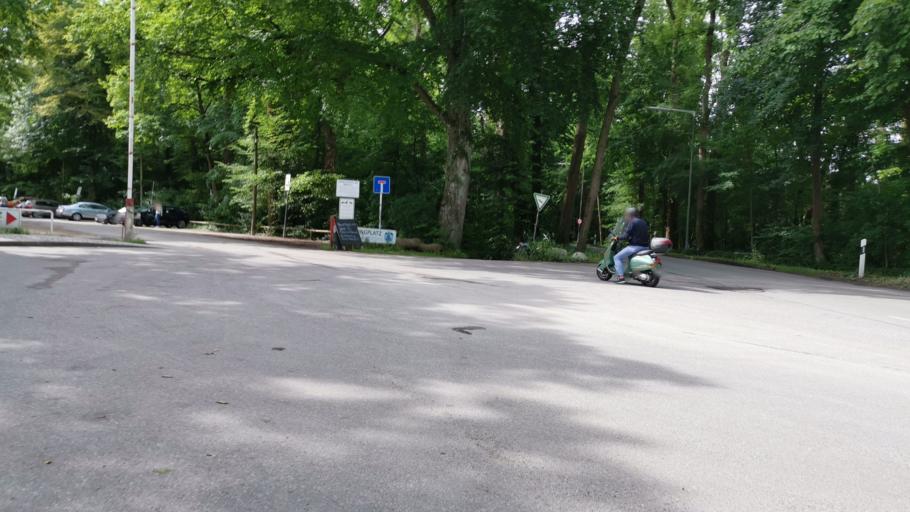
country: DE
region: Bavaria
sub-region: Upper Bavaria
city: Pullach im Isartal
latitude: 48.0918
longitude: 11.5440
